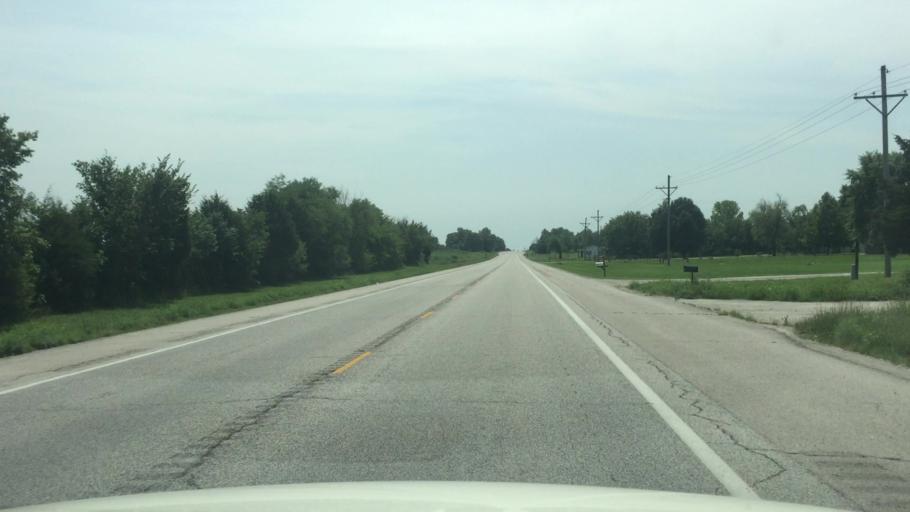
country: US
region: Kansas
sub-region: Cherokee County
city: Galena
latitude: 37.1106
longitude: -94.7044
